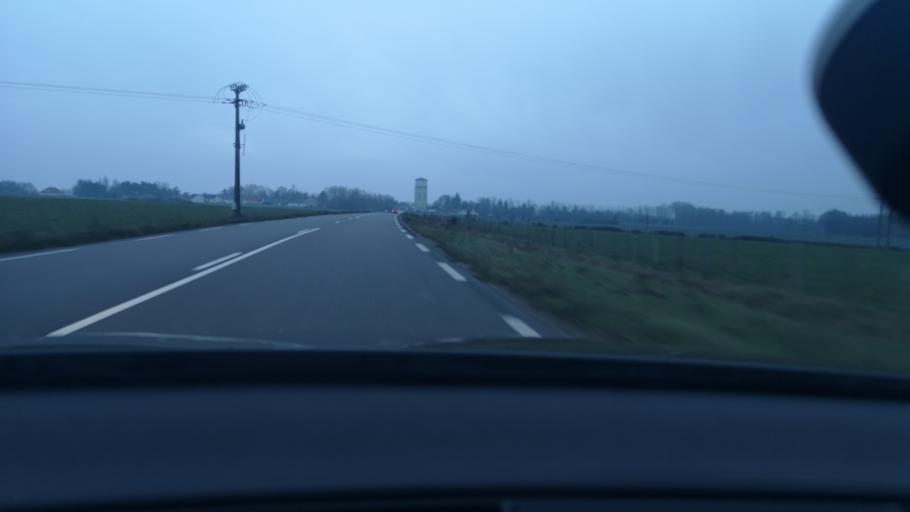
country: FR
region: Bourgogne
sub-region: Departement de la Cote-d'Or
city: Seurre
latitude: 47.0729
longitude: 5.1010
